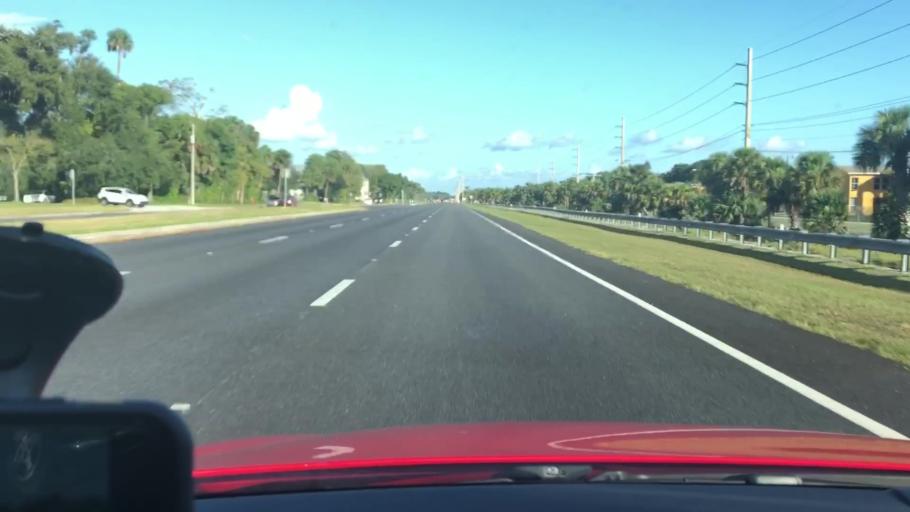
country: US
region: Florida
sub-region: Volusia County
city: Daytona Beach
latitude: 29.1943
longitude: -81.0345
